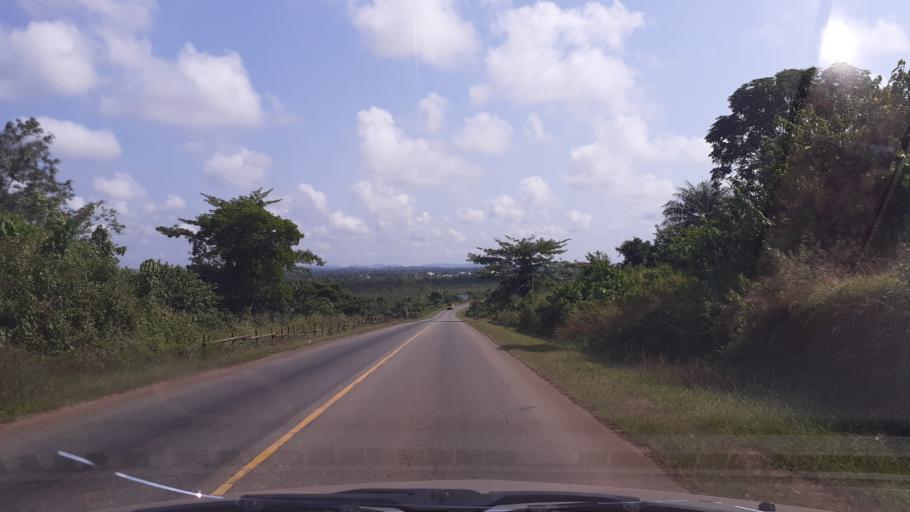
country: LR
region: Montserrado
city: Bensonville City
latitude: 6.2269
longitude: -10.5321
